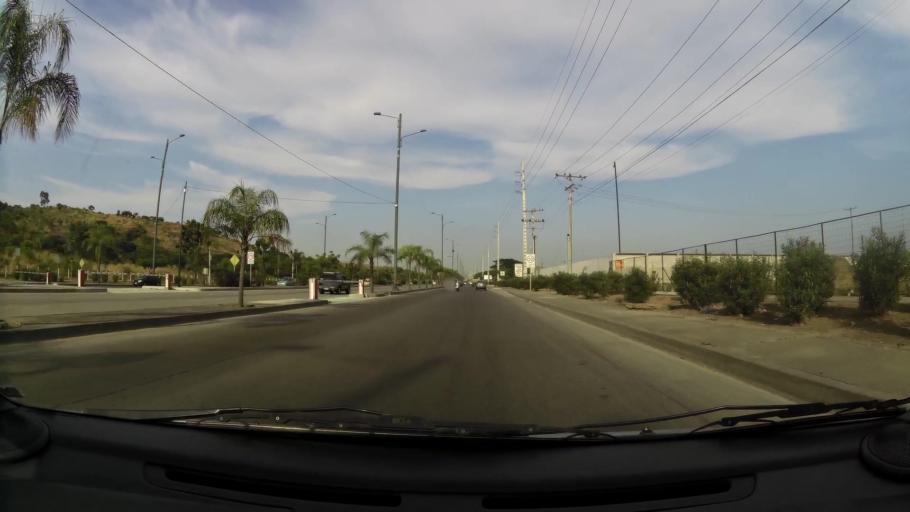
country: EC
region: Guayas
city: Eloy Alfaro
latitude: -2.0682
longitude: -79.9130
